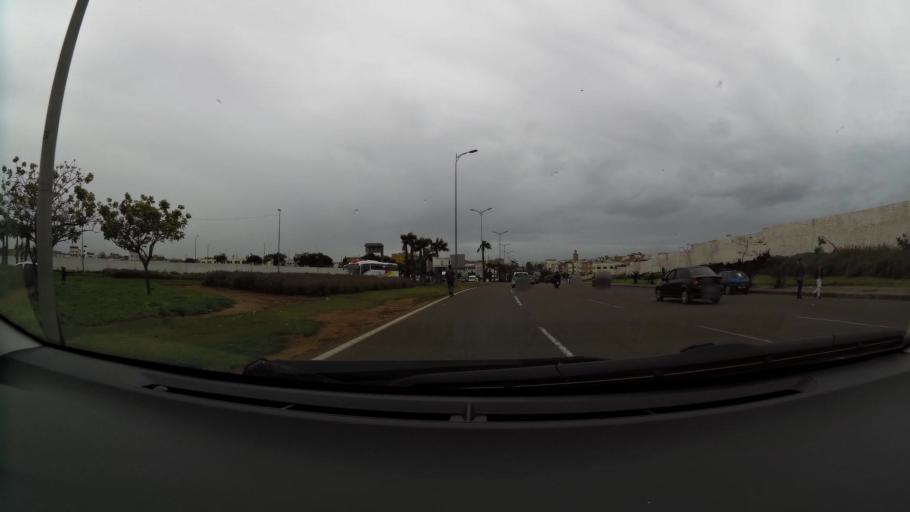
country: MA
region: Grand Casablanca
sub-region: Casablanca
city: Casablanca
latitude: 33.5693
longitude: -7.5760
